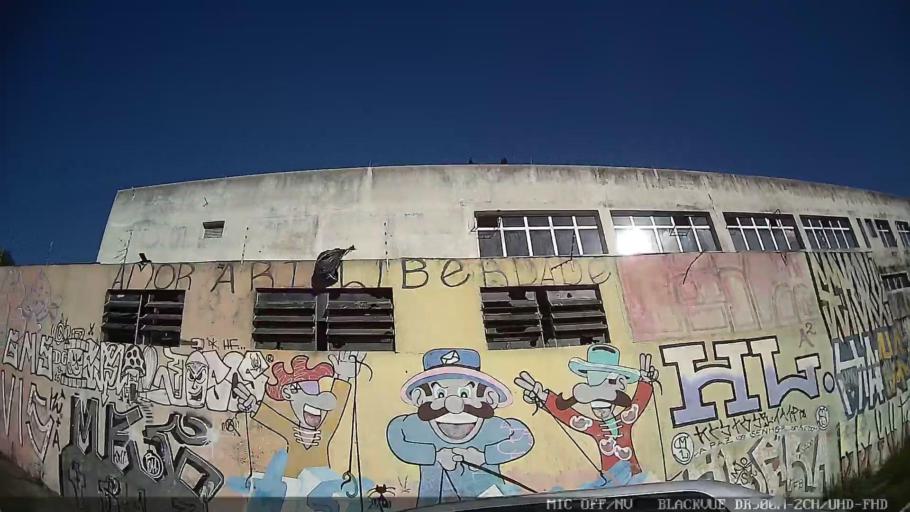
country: BR
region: Sao Paulo
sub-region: Sao Caetano Do Sul
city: Sao Caetano do Sul
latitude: -23.5494
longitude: -46.5229
